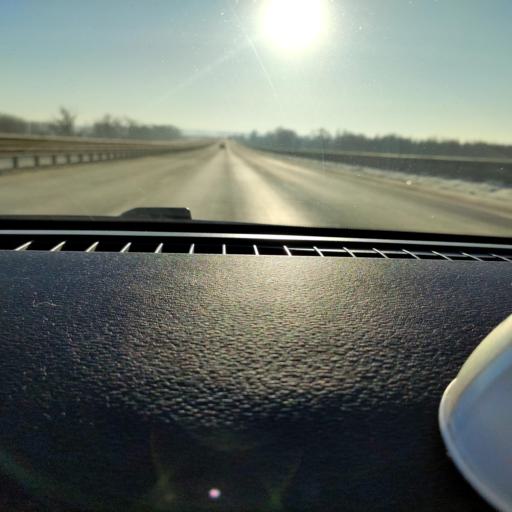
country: RU
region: Samara
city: Smyshlyayevka
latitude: 53.1746
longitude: 50.3132
